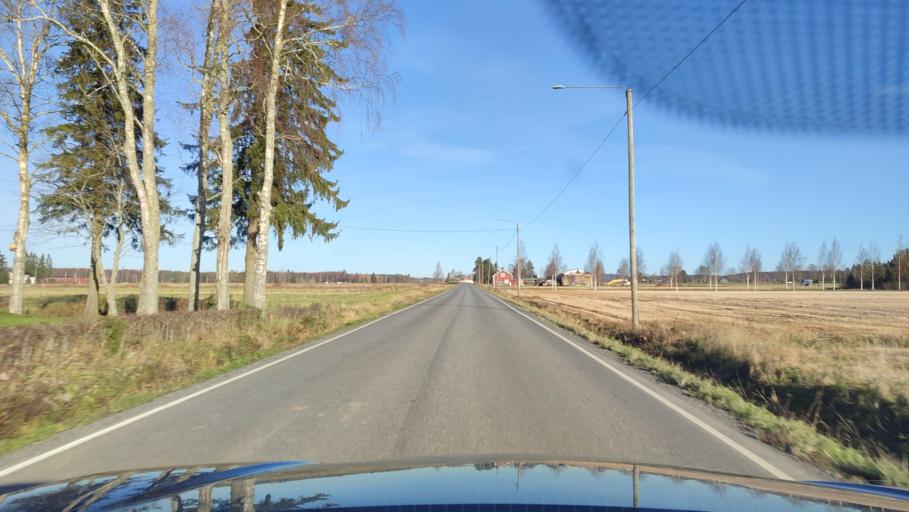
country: FI
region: Southern Ostrobothnia
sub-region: Suupohja
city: Karijoki
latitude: 62.2933
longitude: 21.7190
